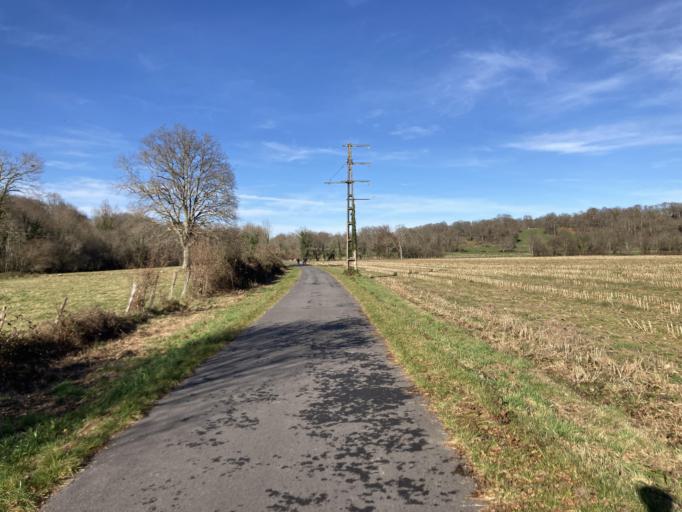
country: FR
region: Aquitaine
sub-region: Departement des Pyrenees-Atlantiques
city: Arudy
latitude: 43.1197
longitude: -0.4380
